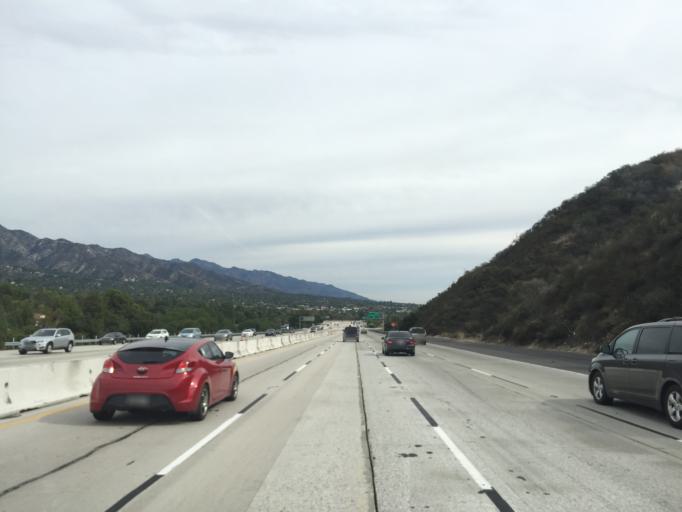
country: US
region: California
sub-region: Los Angeles County
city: La Crescenta-Montrose
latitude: 34.2323
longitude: -118.2713
